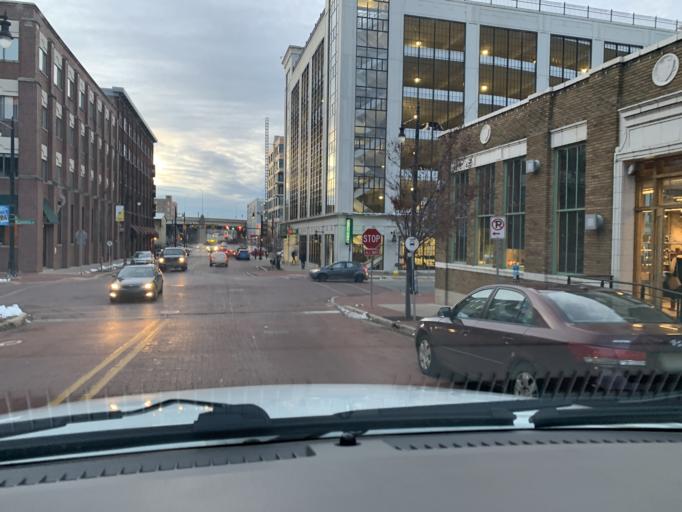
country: US
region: Michigan
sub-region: Kent County
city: Grand Rapids
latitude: 42.9597
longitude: -85.6687
